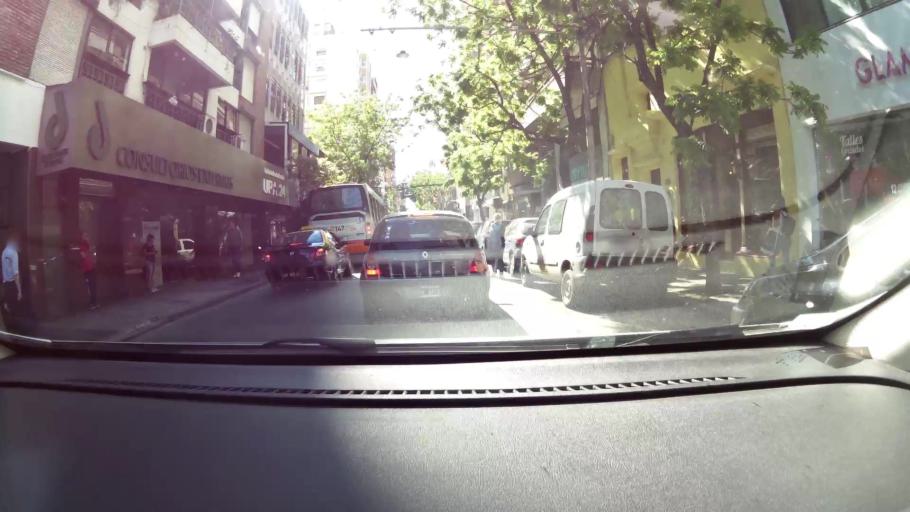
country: AR
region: Santa Fe
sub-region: Departamento de Rosario
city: Rosario
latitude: -32.9504
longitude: -60.6457
